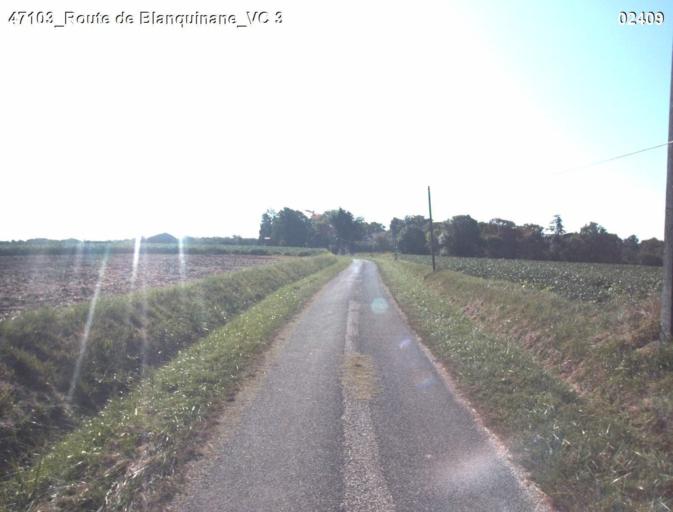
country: FR
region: Aquitaine
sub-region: Departement du Lot-et-Garonne
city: Nerac
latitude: 44.0877
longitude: 0.3372
